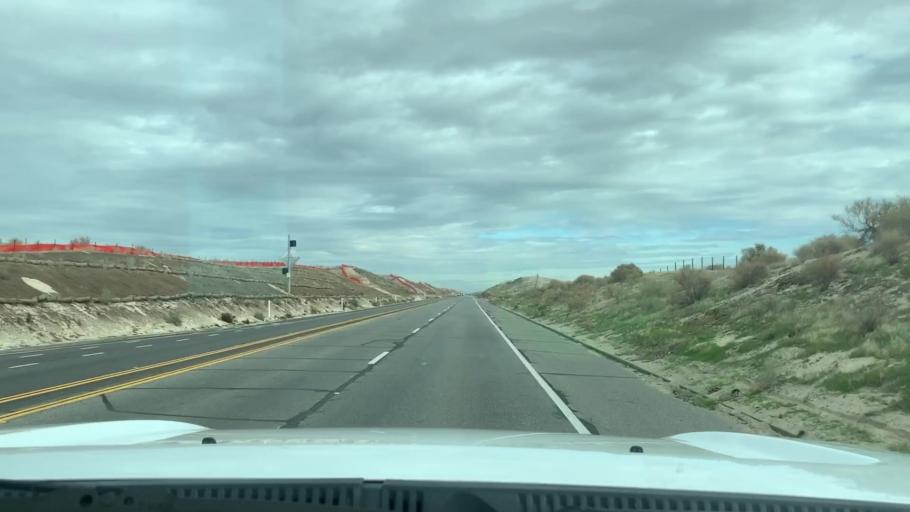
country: US
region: California
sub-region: Kern County
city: Ford City
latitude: 35.2403
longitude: -119.3572
